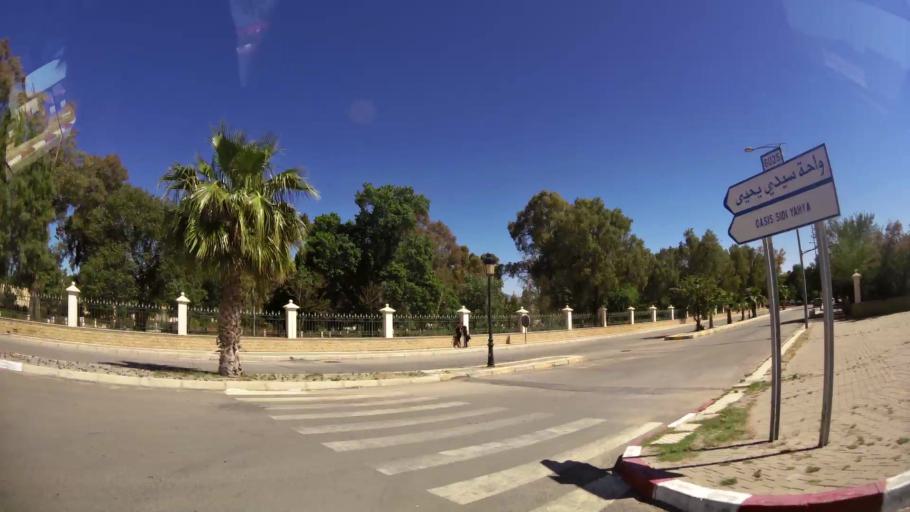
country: MA
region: Oriental
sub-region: Oujda-Angad
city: Oujda
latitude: 34.6671
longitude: -1.8637
